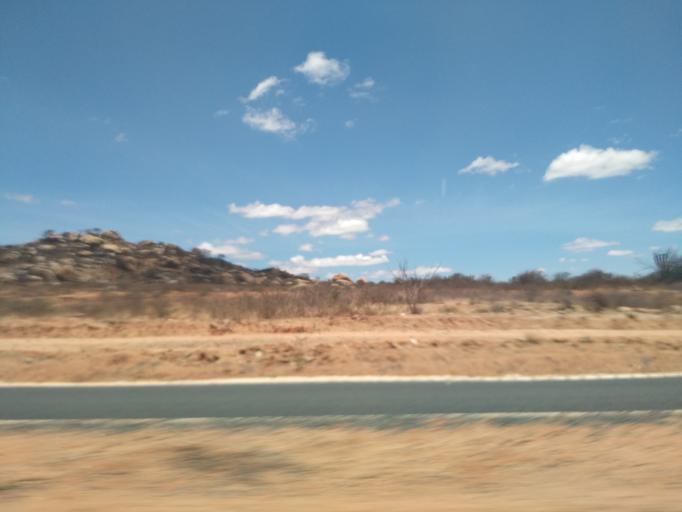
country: TZ
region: Dodoma
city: Kisasa
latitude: -6.1815
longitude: 35.8381
